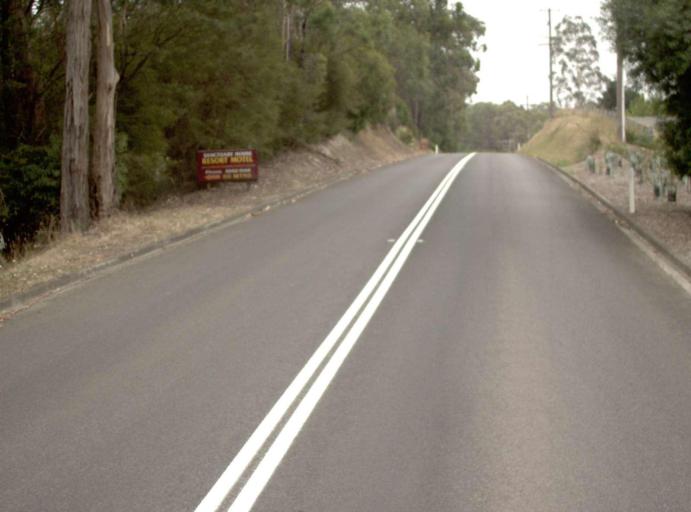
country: AU
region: Victoria
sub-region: Yarra Ranges
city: Badger Creek
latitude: -37.6779
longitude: 145.5329
